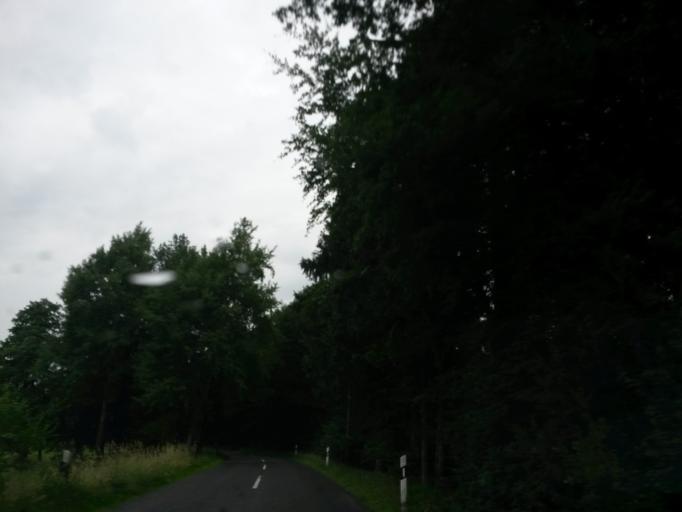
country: DE
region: North Rhine-Westphalia
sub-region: Regierungsbezirk Koln
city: Much
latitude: 50.9285
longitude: 7.3818
